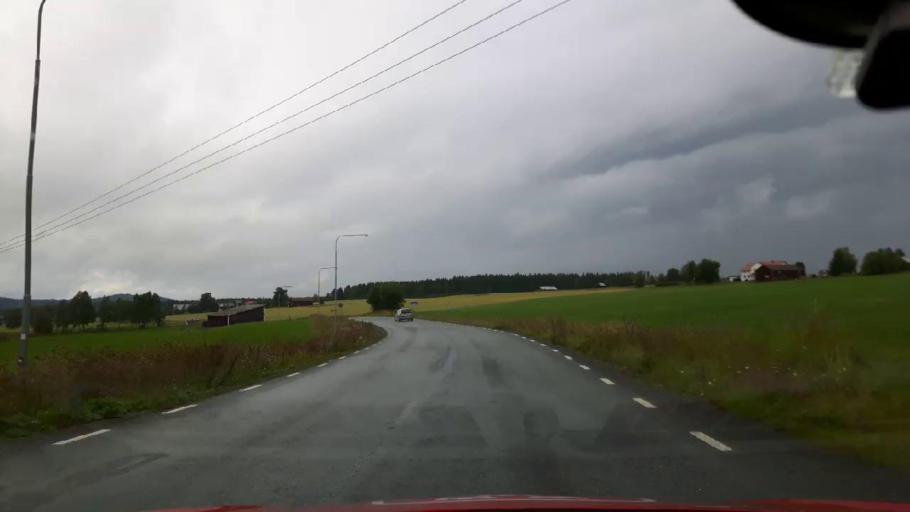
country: SE
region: Jaemtland
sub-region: Krokoms Kommun
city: Krokom
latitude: 63.3568
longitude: 14.1536
